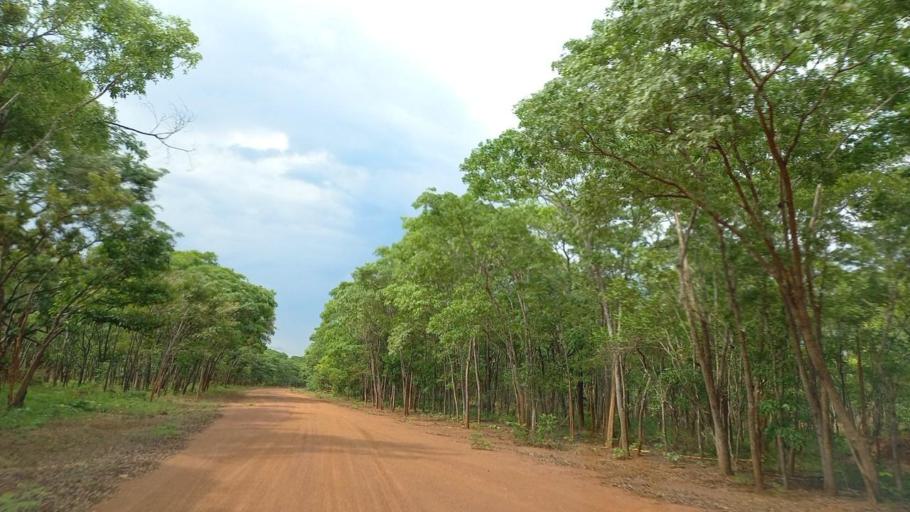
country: ZM
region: North-Western
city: Kalengwa
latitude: -13.4111
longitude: 25.0623
